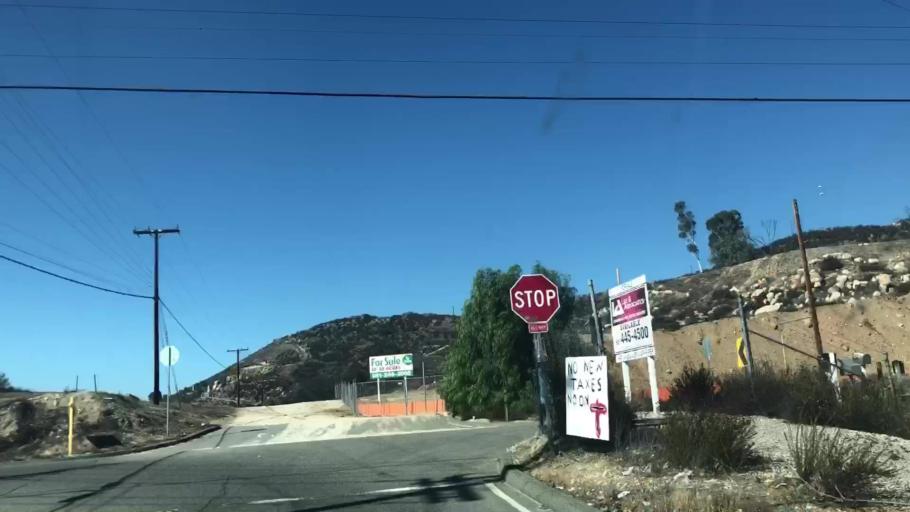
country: US
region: California
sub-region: Riverside County
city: Murrieta Hot Springs
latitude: 33.6051
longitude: -117.1755
